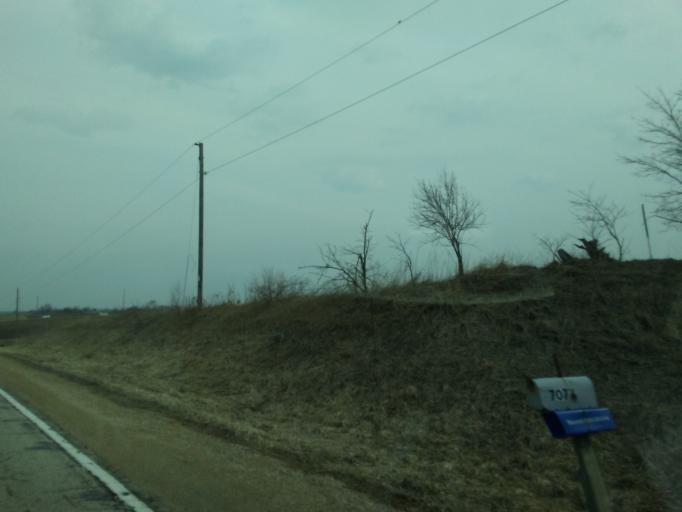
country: US
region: Wisconsin
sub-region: Dane County
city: Waunakee
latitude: 43.2466
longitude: -89.4616
